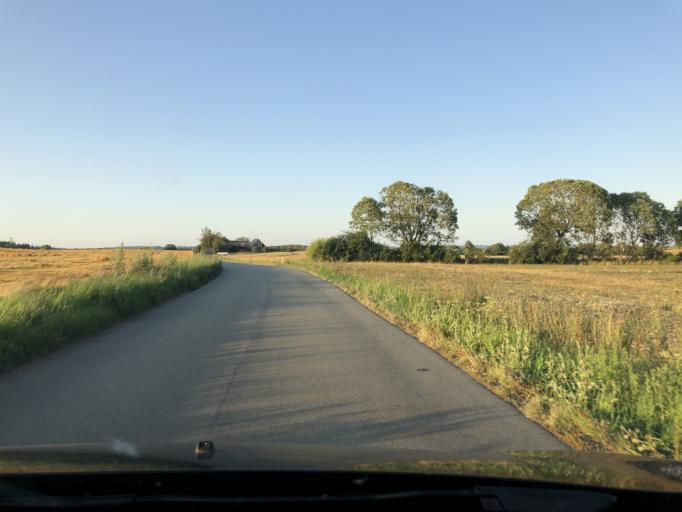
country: DK
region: South Denmark
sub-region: Vejle Kommune
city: Brejning
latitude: 55.6467
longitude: 9.7123
